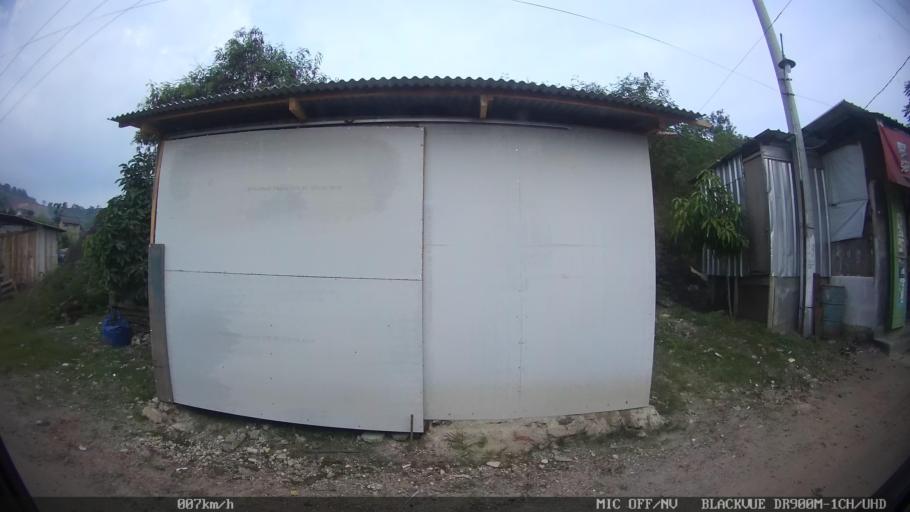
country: ID
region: Lampung
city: Panjang
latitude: -5.4440
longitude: 105.3041
